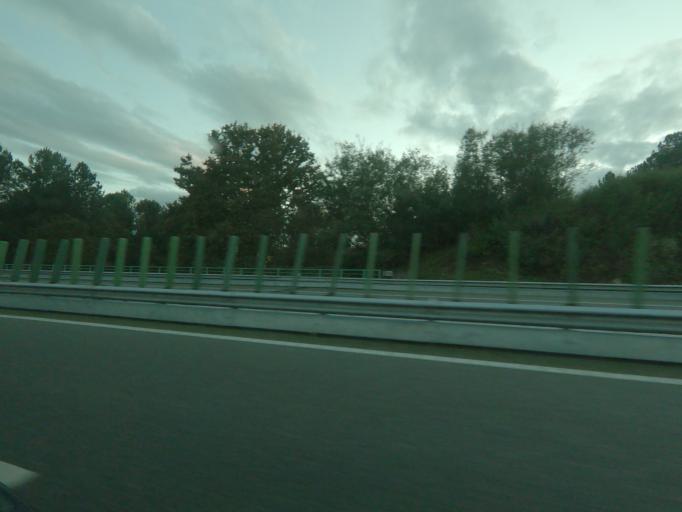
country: PT
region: Porto
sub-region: Marco de Canaveses
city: Marco de Canavezes
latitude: 41.2272
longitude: -8.1742
